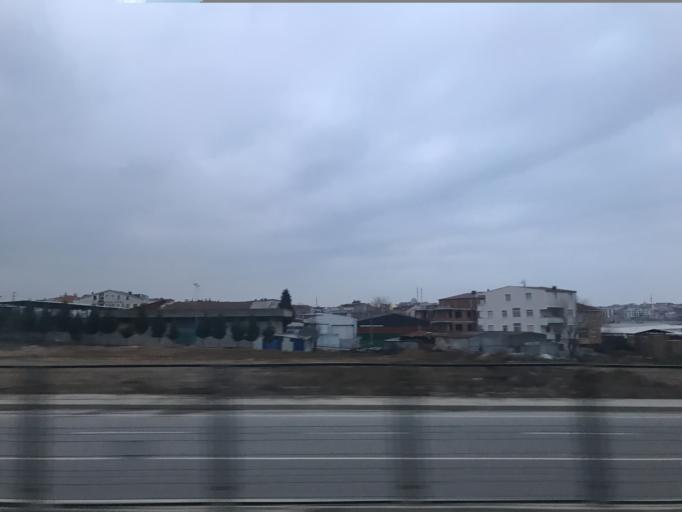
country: TR
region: Kocaeli
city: Darica
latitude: 40.7947
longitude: 29.3867
